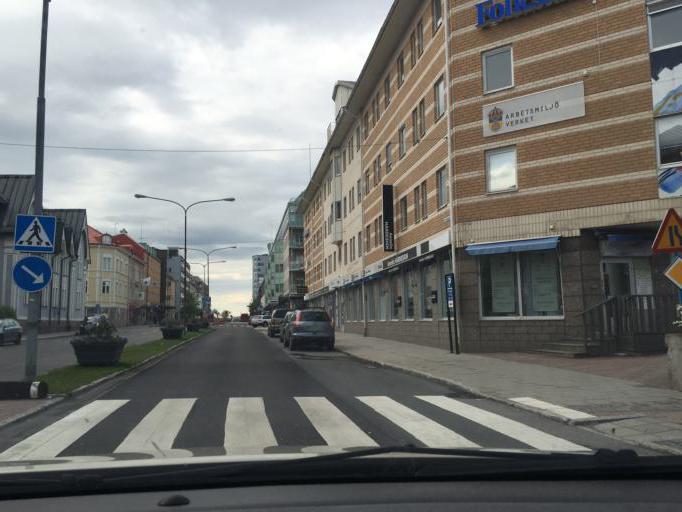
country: SE
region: Norrbotten
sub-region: Lulea Kommun
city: Lulea
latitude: 65.5821
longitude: 22.1536
